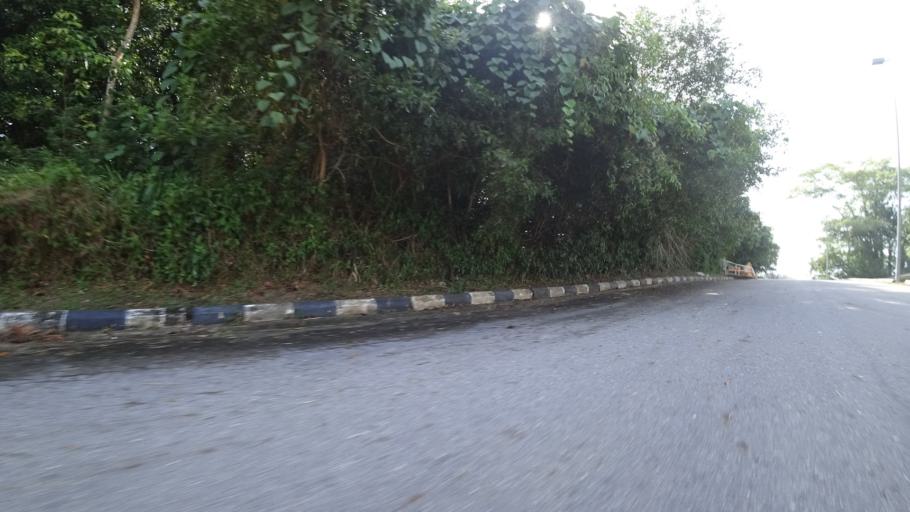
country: BN
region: Brunei and Muara
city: Bandar Seri Begawan
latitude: 4.9483
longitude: 114.8369
